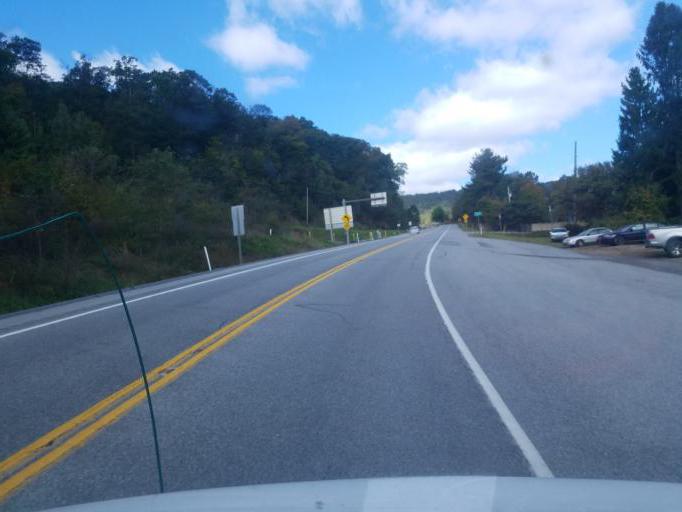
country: US
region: Pennsylvania
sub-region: Fulton County
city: McConnellsburg
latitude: 40.0138
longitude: -78.1173
